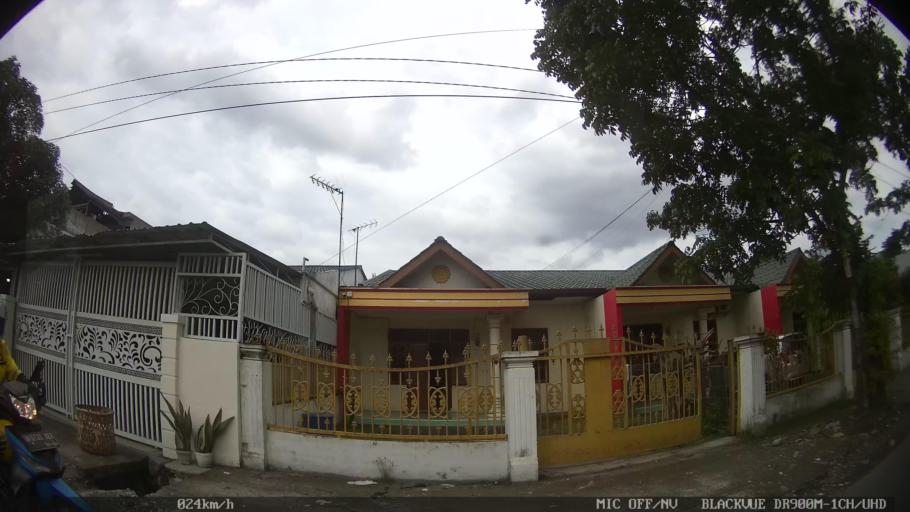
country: ID
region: North Sumatra
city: Sunggal
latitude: 3.5981
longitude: 98.6175
